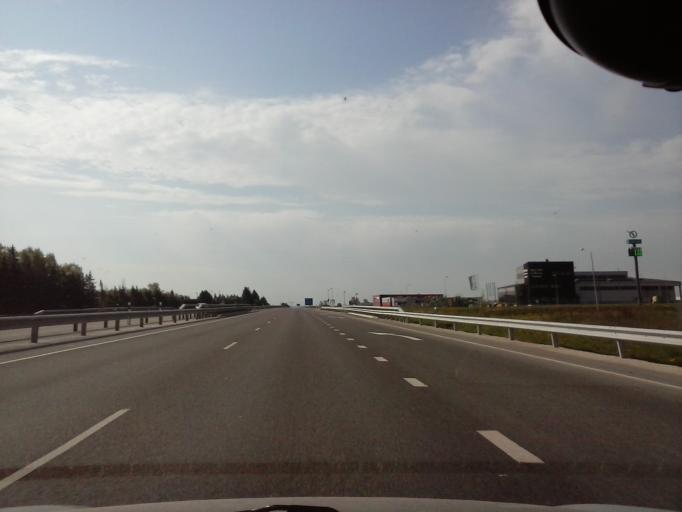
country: EE
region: Tartu
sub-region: UElenurme vald
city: Ulenurme
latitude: 58.3231
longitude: 26.7166
